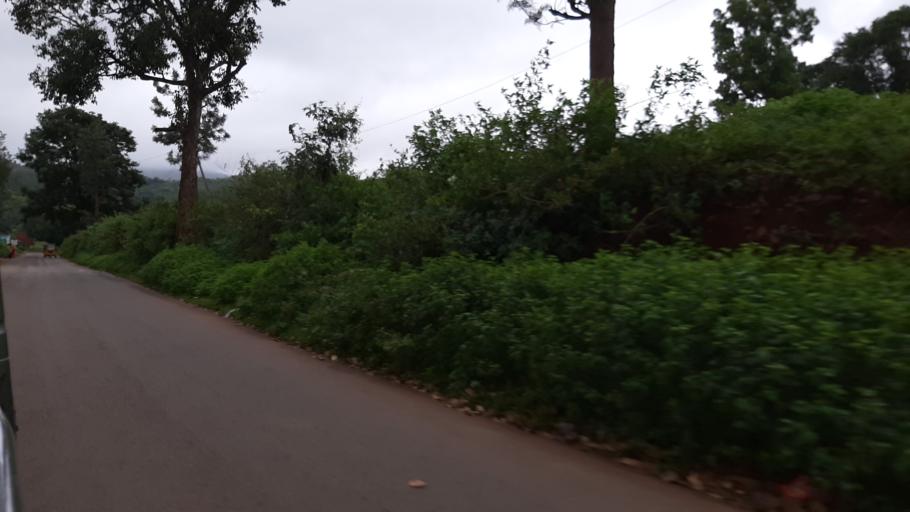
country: IN
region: Andhra Pradesh
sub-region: Vizianagaram District
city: Salur
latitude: 18.2861
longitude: 82.9388
